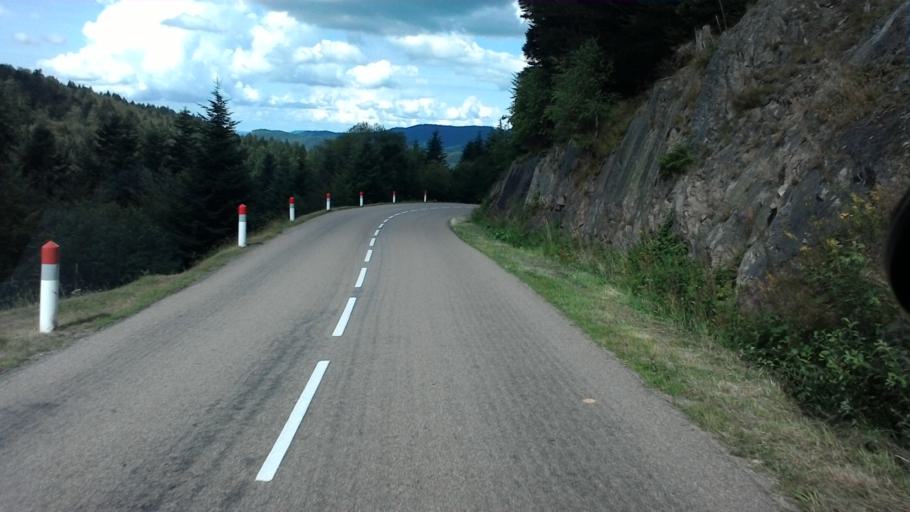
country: FR
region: Lorraine
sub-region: Departement des Vosges
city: La Bresse
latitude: 48.0307
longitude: 6.8698
